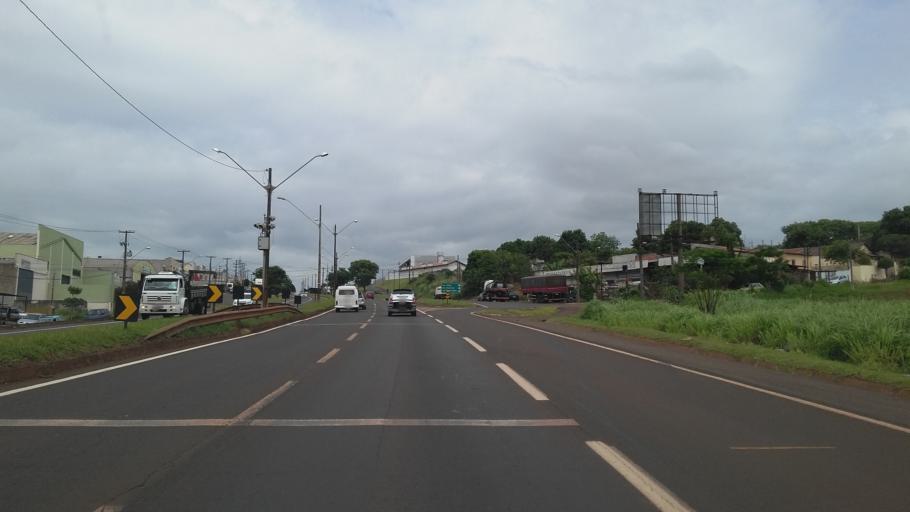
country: BR
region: Parana
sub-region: Londrina
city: Londrina
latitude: -23.2931
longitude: -51.1180
